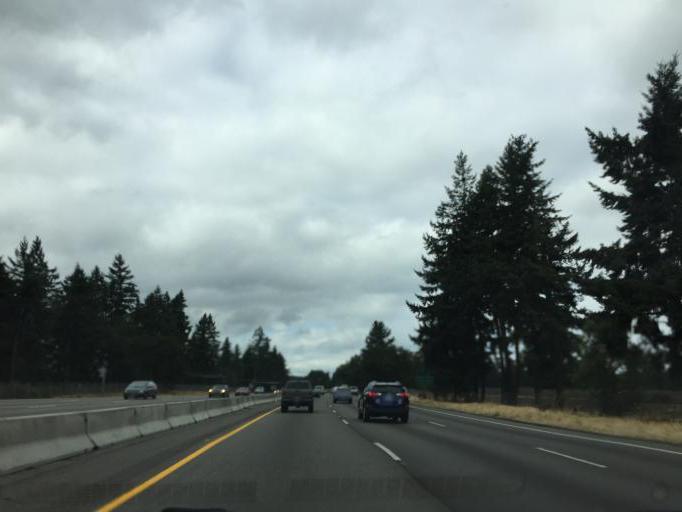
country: US
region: Washington
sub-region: Pierce County
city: Fort Lewis
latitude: 47.1101
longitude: -122.5723
